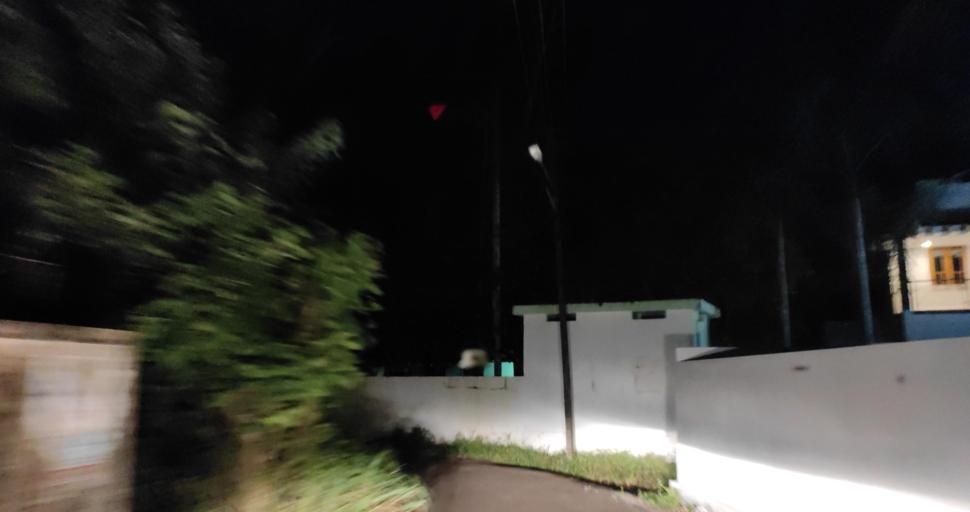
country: IN
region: Kerala
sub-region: Alappuzha
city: Shertallai
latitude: 9.6162
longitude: 76.3360
